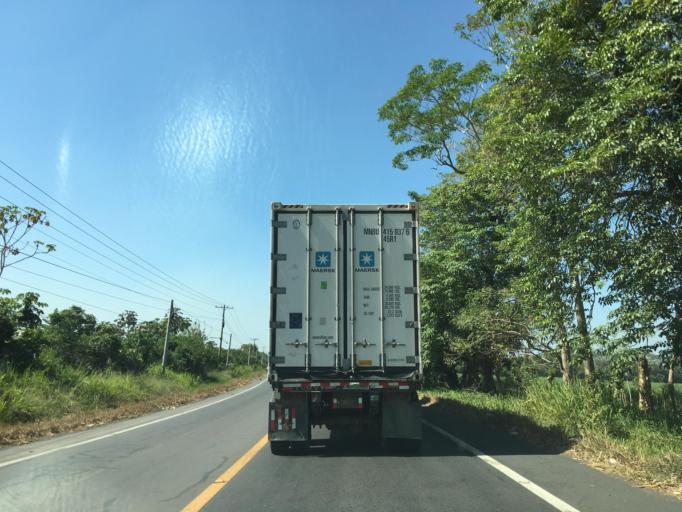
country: GT
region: Escuintla
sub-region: Municipio de Masagua
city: Masagua
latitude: 14.1880
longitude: -90.8597
